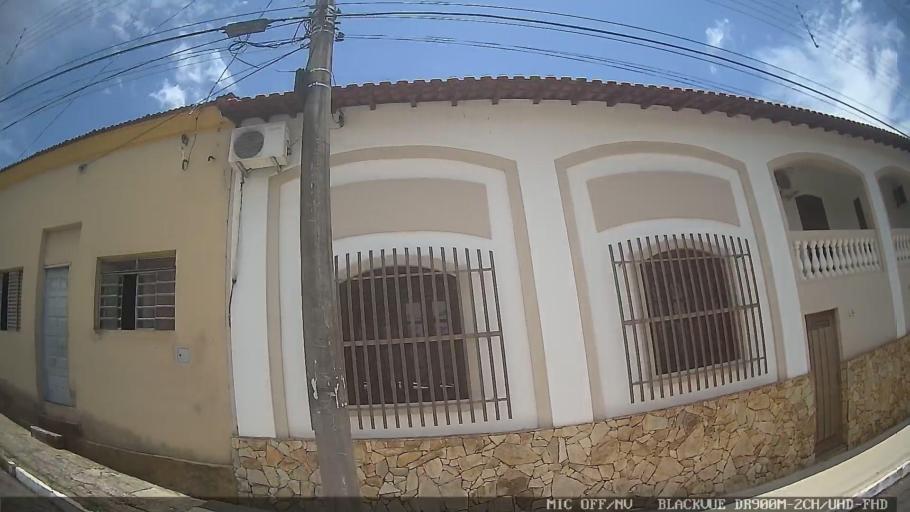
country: BR
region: Sao Paulo
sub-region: Laranjal Paulista
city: Laranjal Paulista
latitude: -23.0495
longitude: -47.8378
